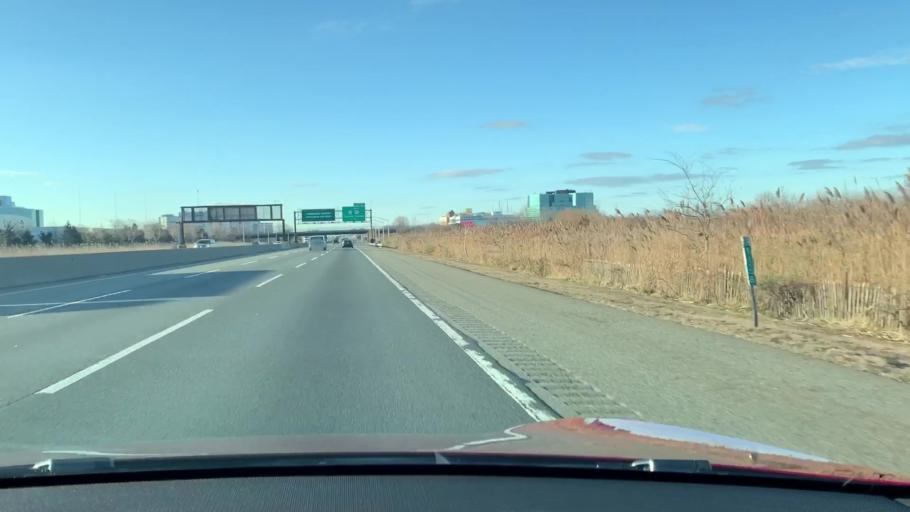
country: US
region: New Jersey
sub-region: Hudson County
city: Secaucus
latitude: 40.7951
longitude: -74.0426
